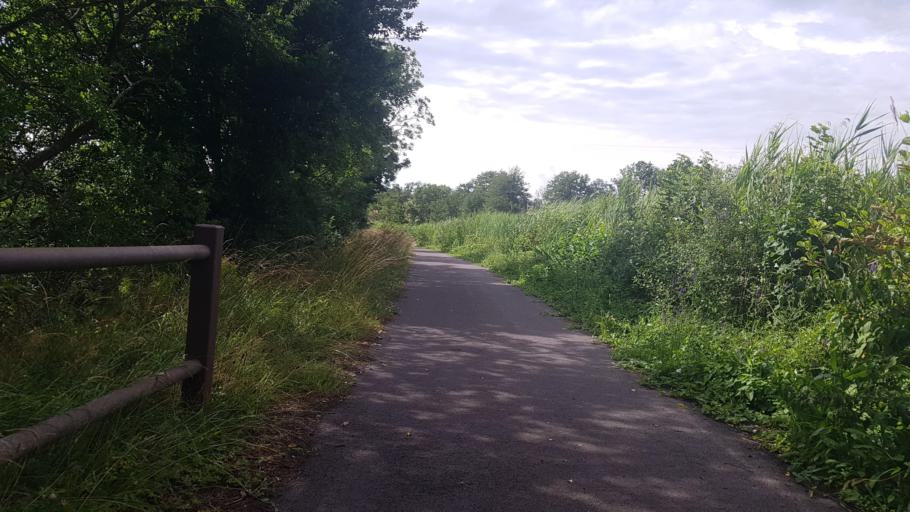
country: FR
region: Lorraine
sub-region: Departement de la Moselle
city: Dieuze
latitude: 48.6902
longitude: 6.7611
